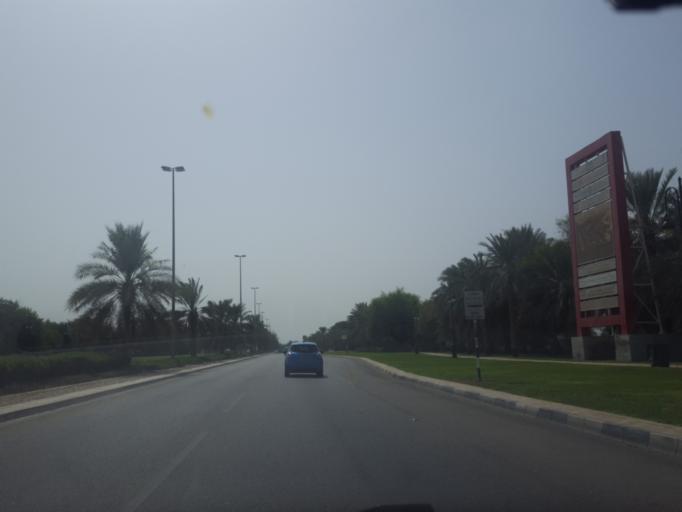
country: AE
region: Abu Dhabi
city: Al Ain
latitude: 24.2057
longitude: 55.7956
